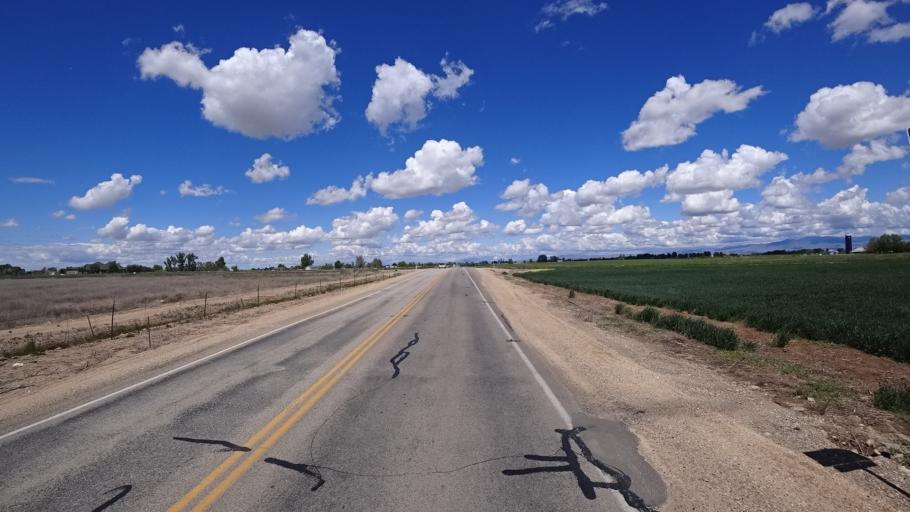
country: US
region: Idaho
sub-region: Ada County
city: Meridian
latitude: 43.5627
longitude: -116.4336
